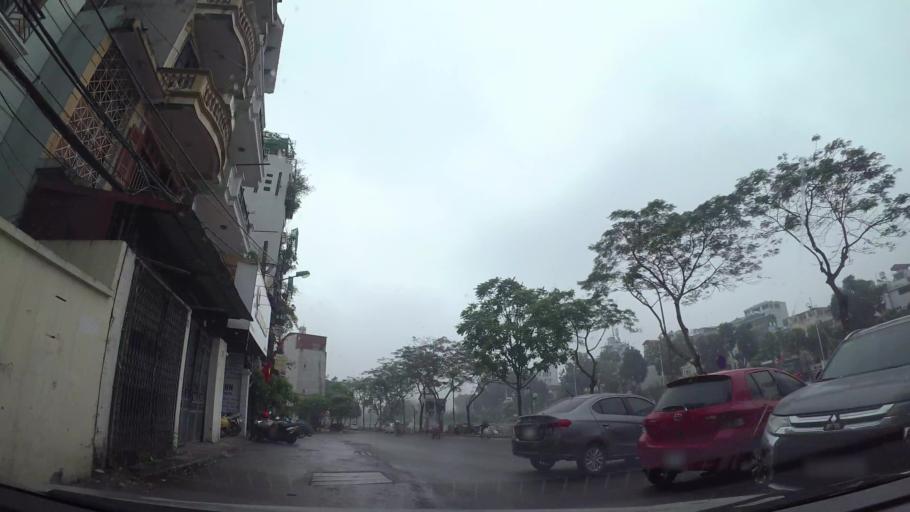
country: VN
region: Ha Noi
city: Cau Giay
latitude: 21.0222
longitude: 105.7994
